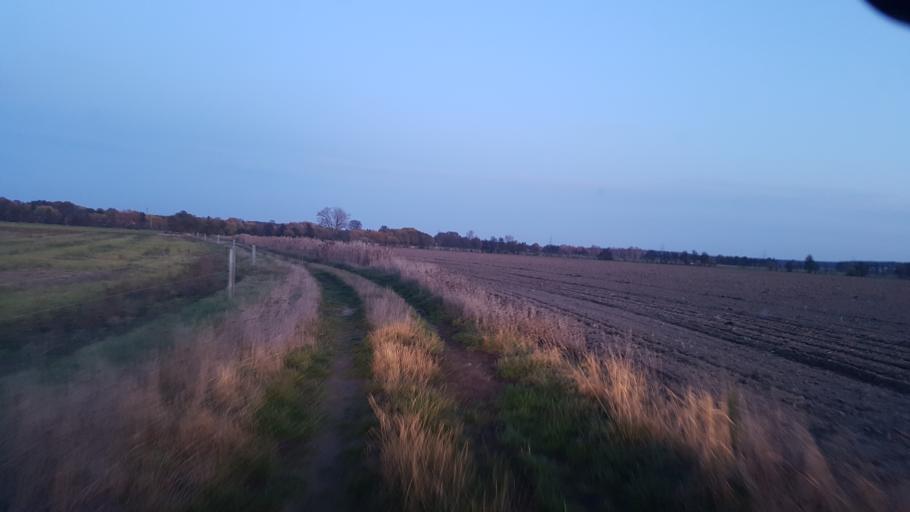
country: DE
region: Brandenburg
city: Schilda
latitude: 51.6205
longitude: 13.3420
